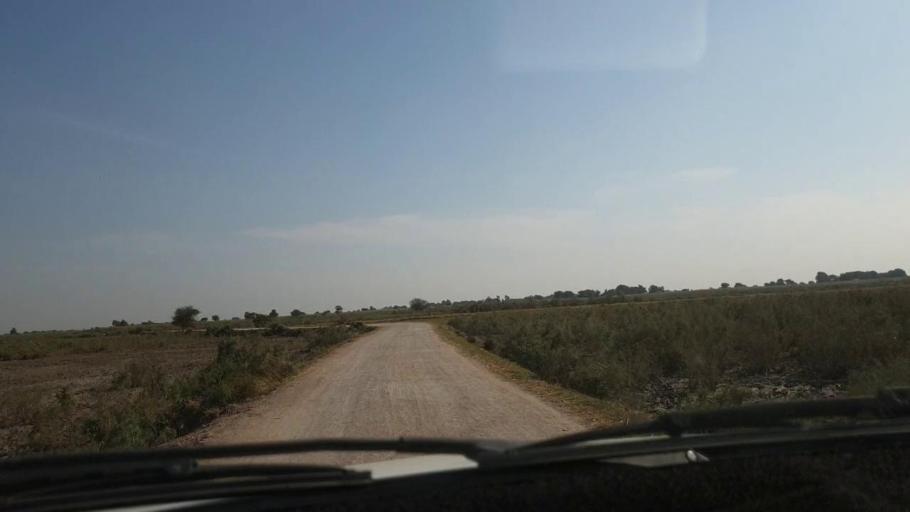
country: PK
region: Sindh
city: Bulri
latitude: 24.9514
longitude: 68.4223
